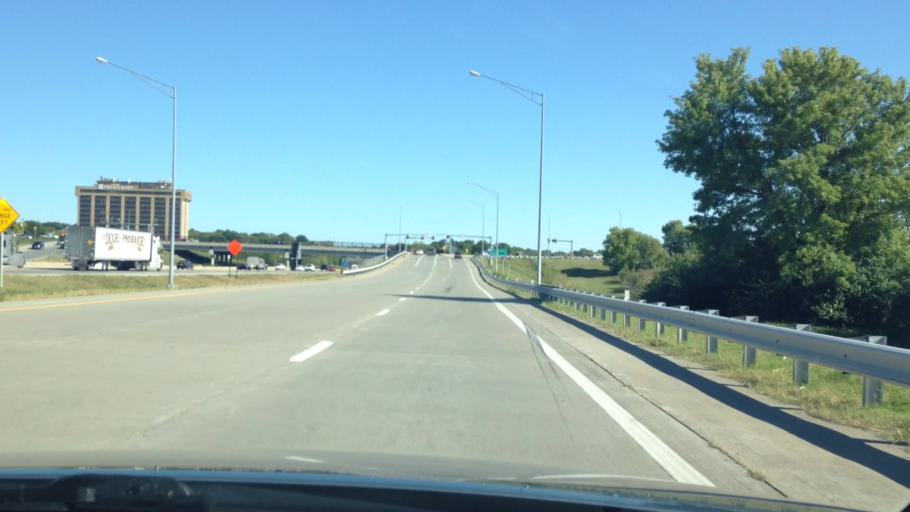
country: US
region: Missouri
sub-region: Jackson County
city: Raytown
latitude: 39.0527
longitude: -94.4778
